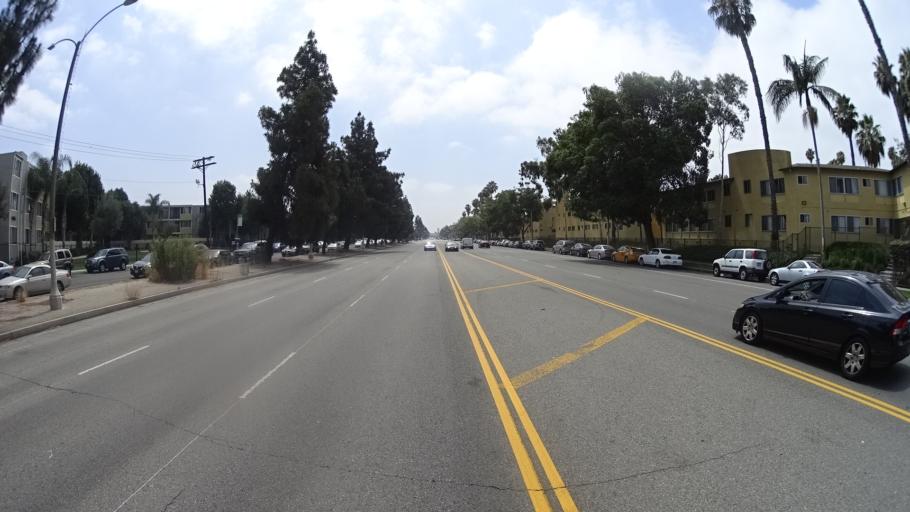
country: US
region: California
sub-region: Los Angeles County
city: View Park-Windsor Hills
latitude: 34.0189
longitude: -118.3482
